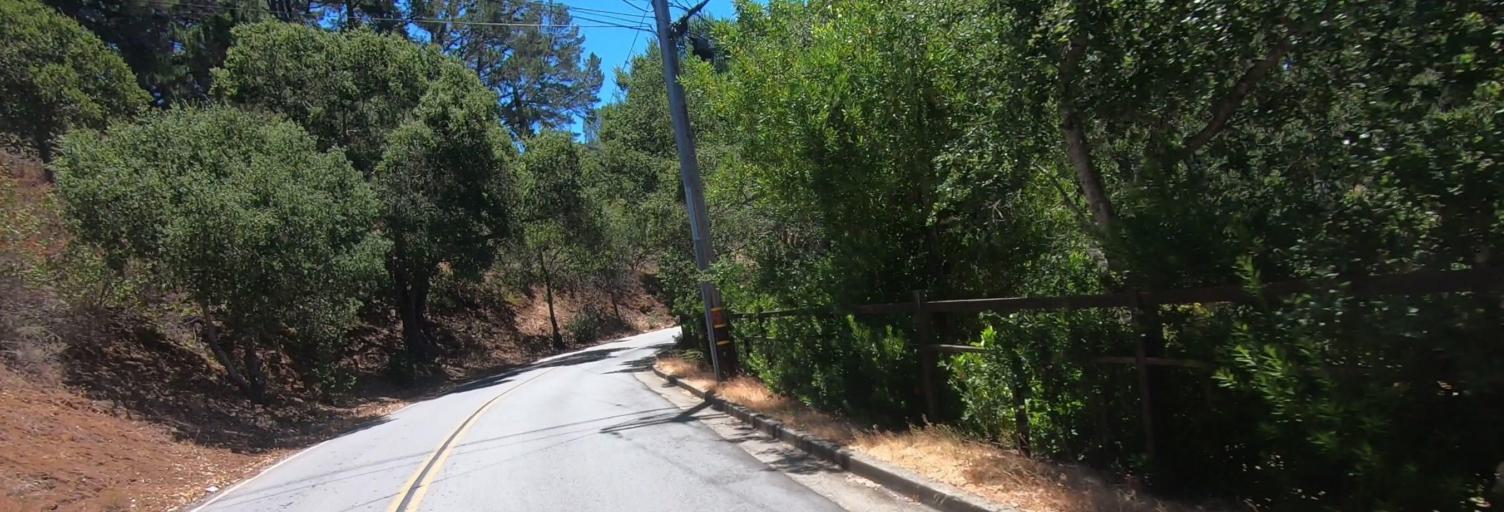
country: US
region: California
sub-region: Santa Clara County
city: Los Altos Hills
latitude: 37.3662
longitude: -122.1673
